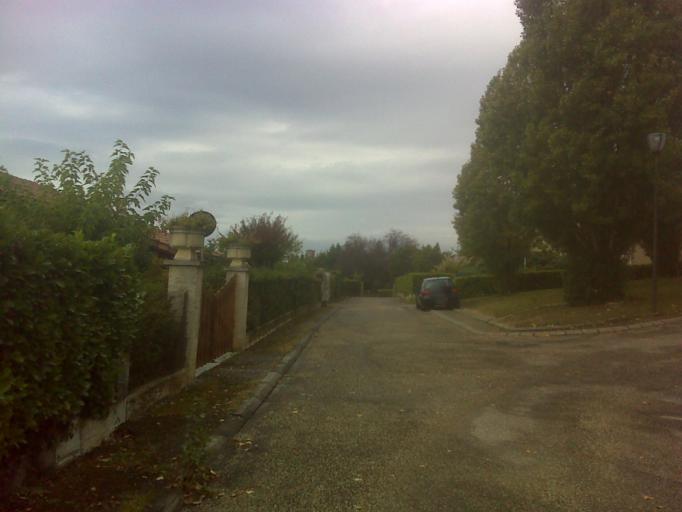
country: FR
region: Midi-Pyrenees
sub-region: Departement du Gers
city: Lectoure
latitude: 43.9326
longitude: 0.6385
